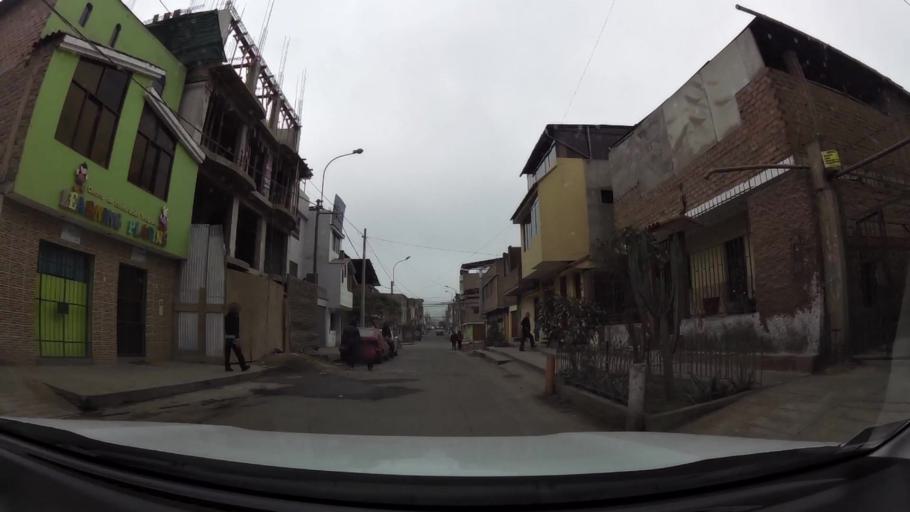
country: PE
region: Lima
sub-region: Lima
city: Surco
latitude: -12.1677
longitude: -76.9461
